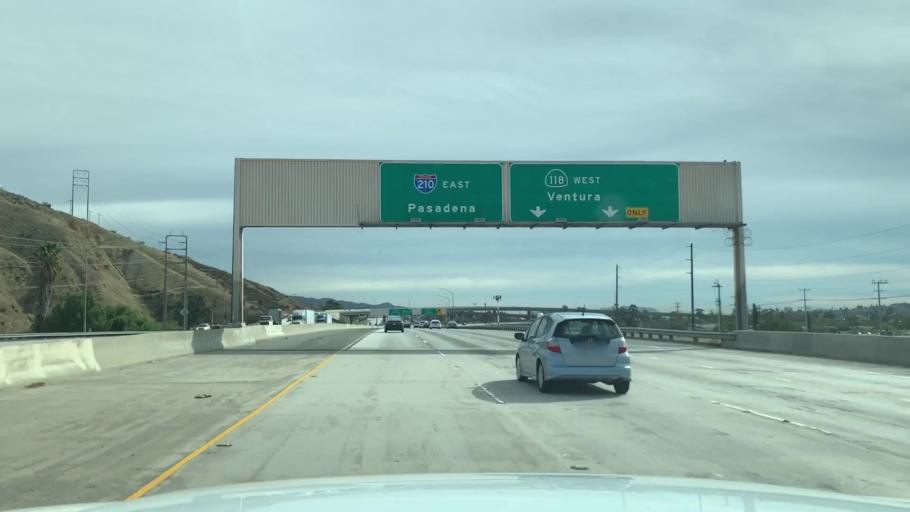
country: US
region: California
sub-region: Los Angeles County
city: San Fernando
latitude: 34.2935
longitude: -118.4134
